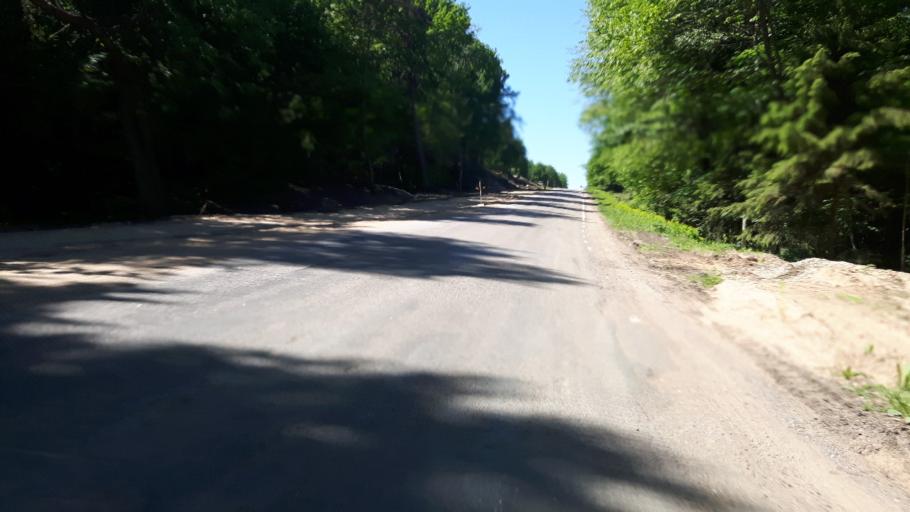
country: EE
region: Ida-Virumaa
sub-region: Narva-Joesuu linn
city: Narva-Joesuu
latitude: 59.4146
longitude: 27.9600
